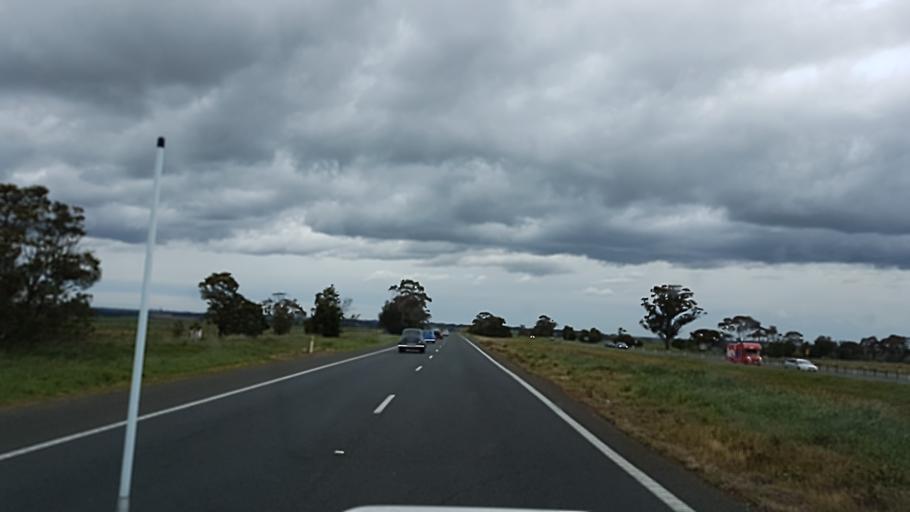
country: AU
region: Victoria
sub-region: Moorabool
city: Bacchus Marsh
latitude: -37.6009
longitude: 144.2732
